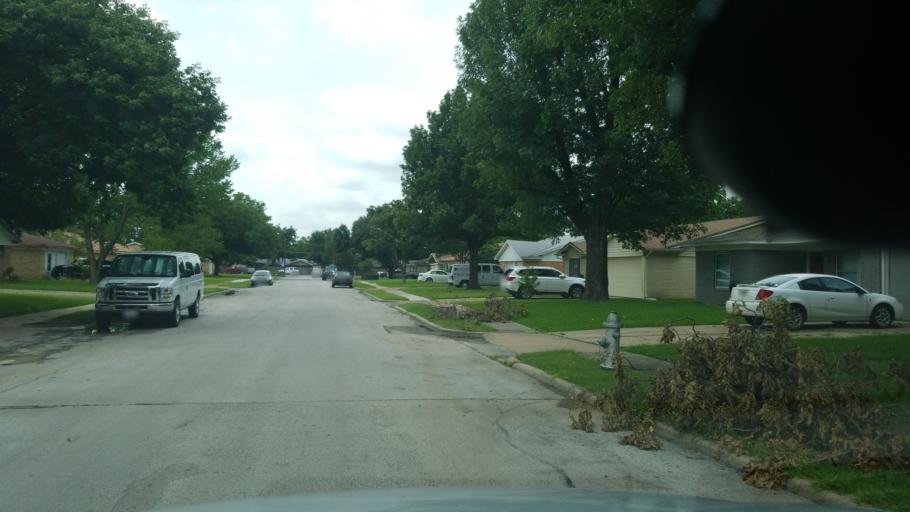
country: US
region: Texas
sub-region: Dallas County
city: Irving
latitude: 32.8458
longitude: -96.9620
